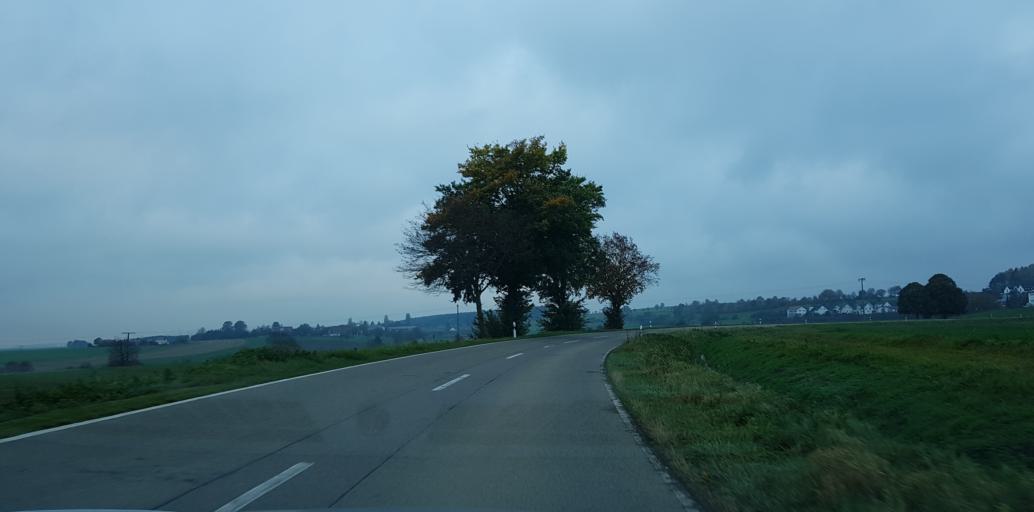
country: DE
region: Baden-Wuerttemberg
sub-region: Tuebingen Region
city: Altheim
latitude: 48.3124
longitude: 9.7815
